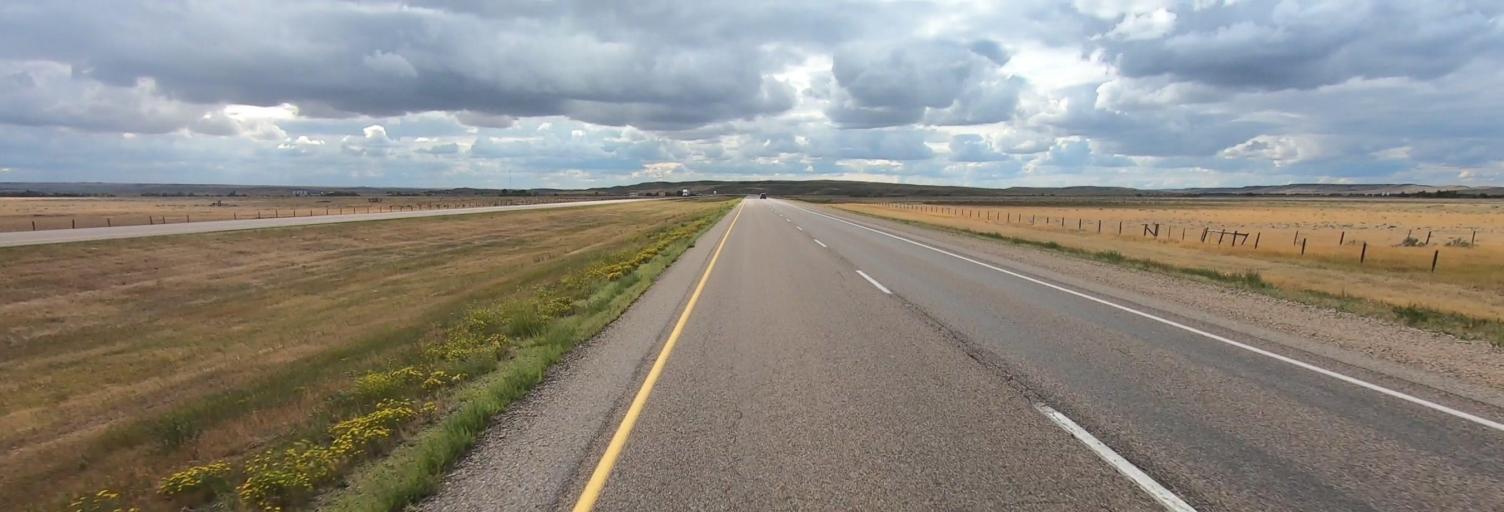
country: CA
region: Saskatchewan
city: Maple Creek
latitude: 49.9608
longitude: -109.9753
